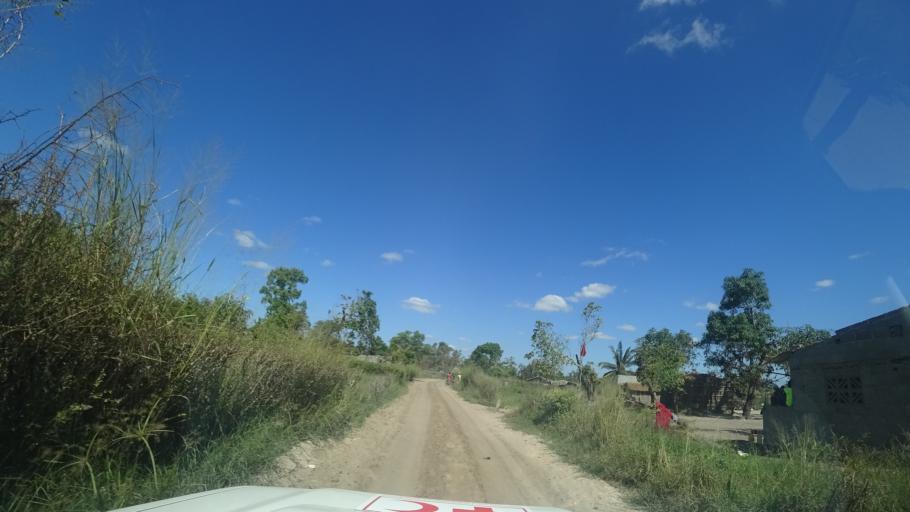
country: MZ
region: Sofala
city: Dondo
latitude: -19.4877
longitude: 34.5993
